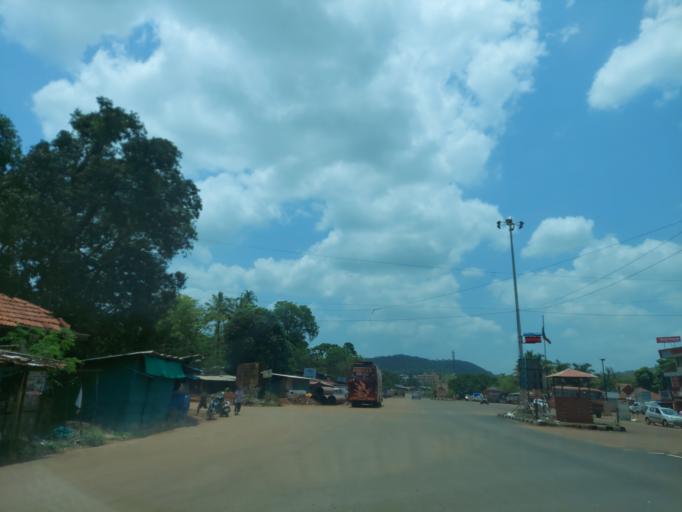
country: IN
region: Maharashtra
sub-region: Sindhudurg
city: Savantvadi
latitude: 15.8174
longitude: 73.8647
